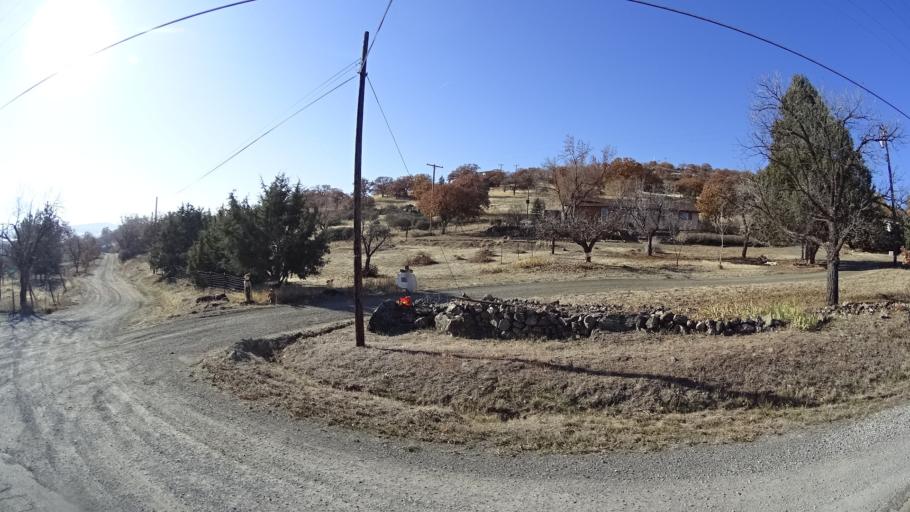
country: US
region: California
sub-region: Siskiyou County
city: Yreka
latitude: 41.7384
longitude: -122.6064
